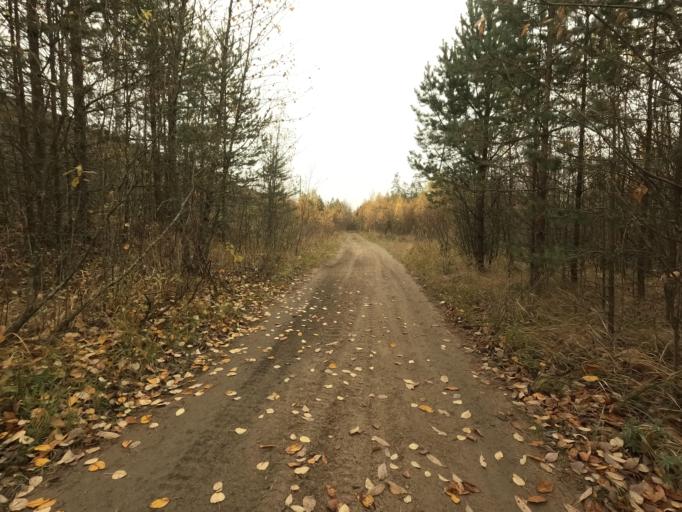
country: RU
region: Leningrad
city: Pavlovo
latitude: 59.7754
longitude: 30.9018
